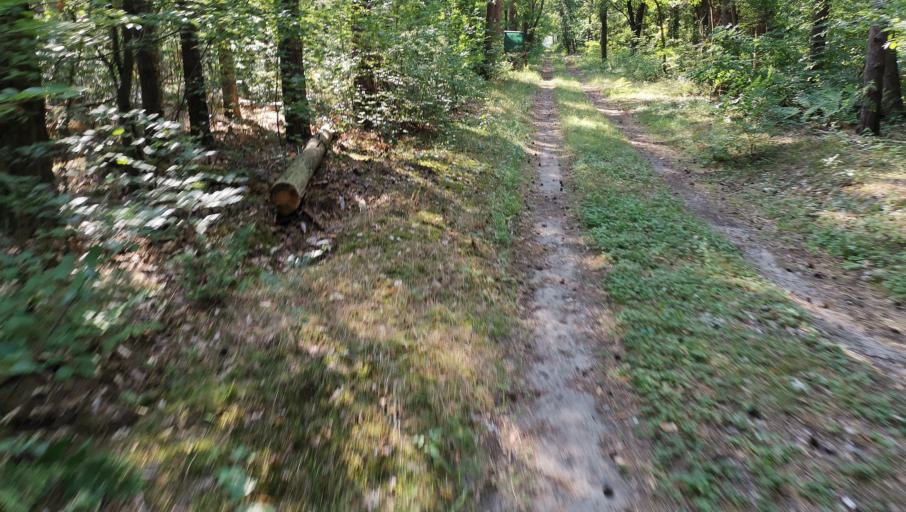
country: DE
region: Brandenburg
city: Werder
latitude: 52.3769
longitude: 12.9996
